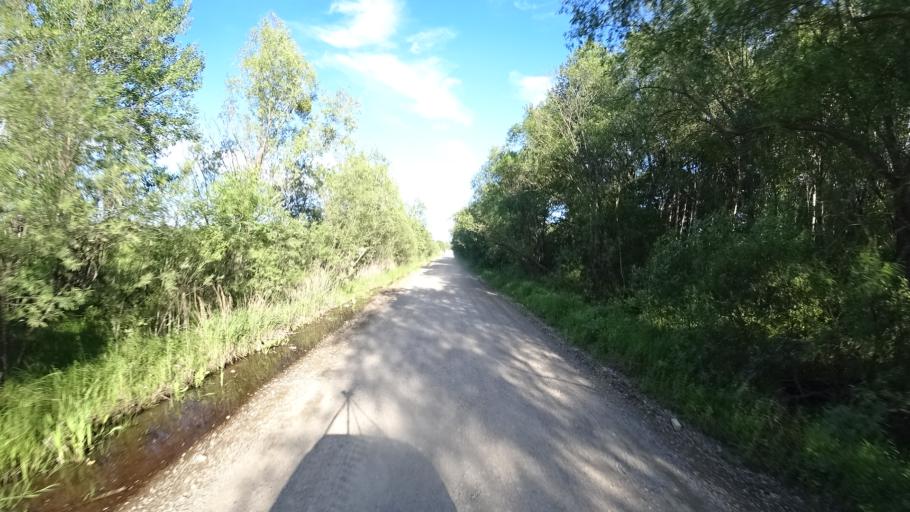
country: RU
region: Khabarovsk Krai
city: Khor
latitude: 47.8430
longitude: 134.9530
